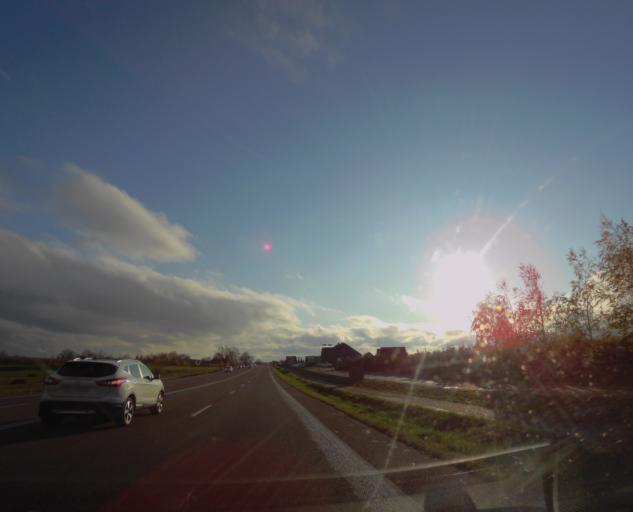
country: PL
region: Subcarpathian Voivodeship
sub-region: Powiat przemyski
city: Orly
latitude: 49.8496
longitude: 22.8038
